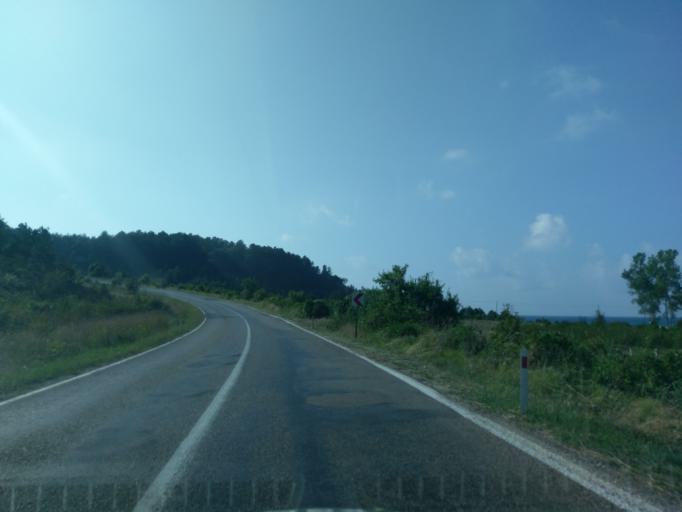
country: TR
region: Sinop
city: Yenikonak
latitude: 41.9411
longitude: 34.7185
